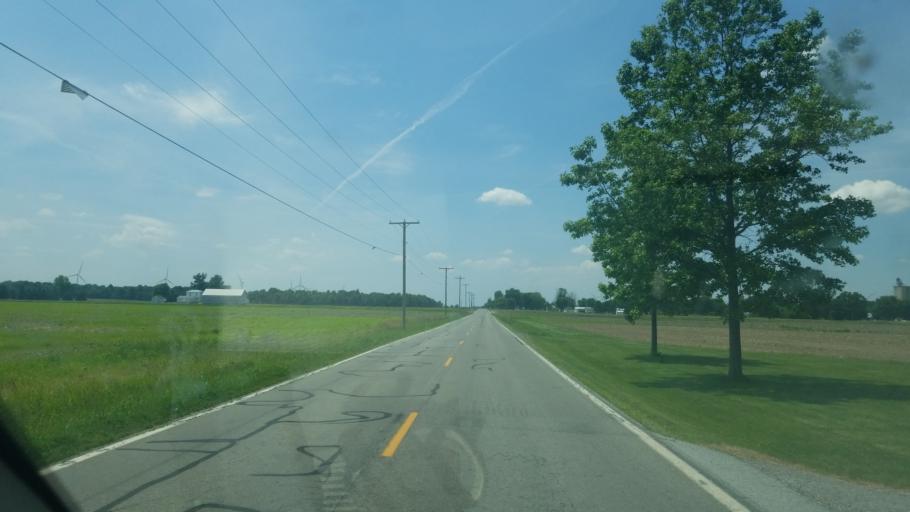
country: US
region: Ohio
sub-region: Hancock County
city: Arlington
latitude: 40.7798
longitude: -83.6838
